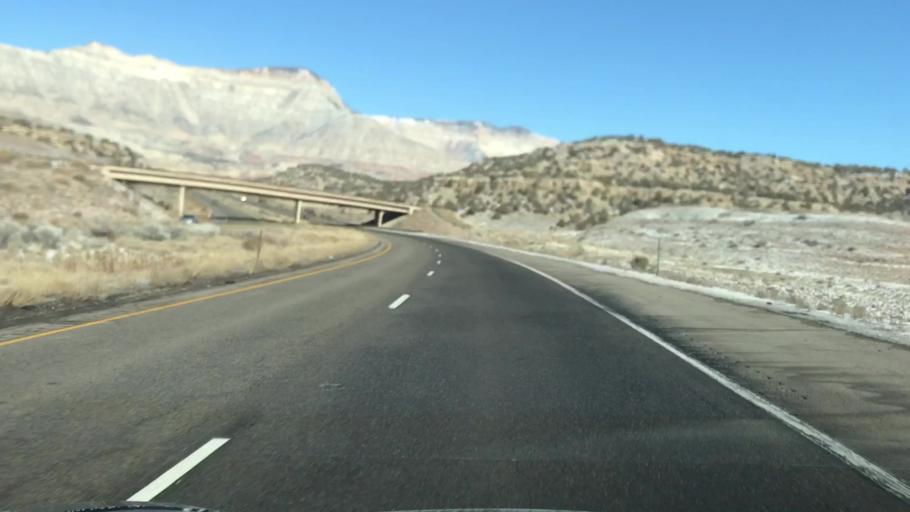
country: US
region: Colorado
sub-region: Garfield County
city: Parachute
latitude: 39.3561
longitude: -108.1705
